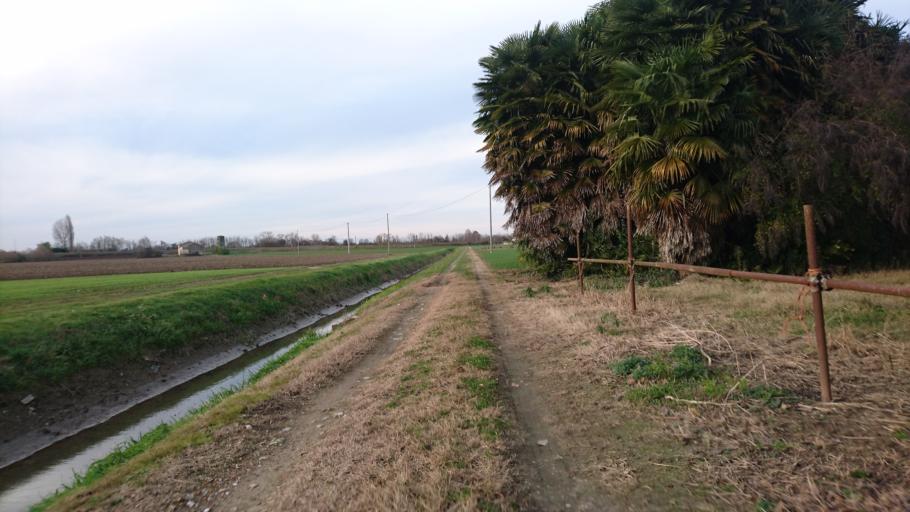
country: IT
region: Veneto
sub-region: Provincia di Padova
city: Polverara
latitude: 45.3250
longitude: 11.9489
